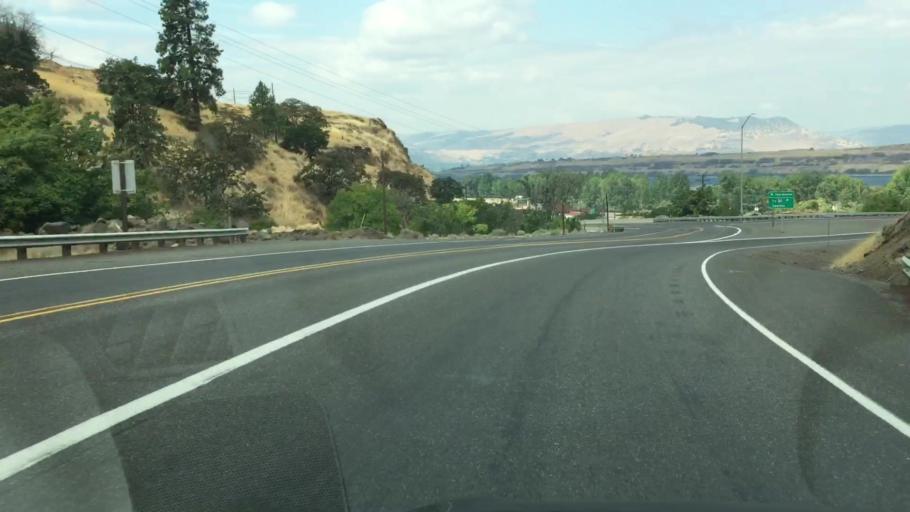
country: US
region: Oregon
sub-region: Wasco County
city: The Dalles
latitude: 45.5981
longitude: -121.1384
